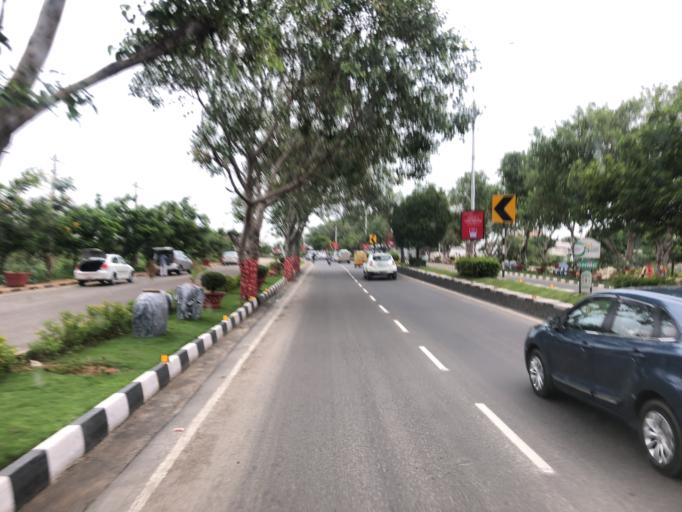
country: IN
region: Telangana
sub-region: Rangareddi
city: Kukatpalli
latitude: 17.4618
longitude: 78.3765
